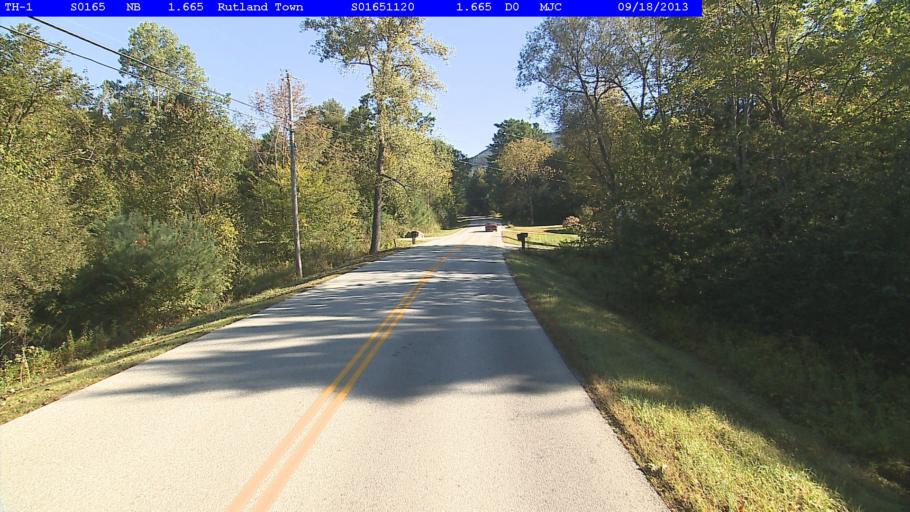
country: US
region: Vermont
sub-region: Rutland County
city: Rutland
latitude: 43.6635
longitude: -72.9490
